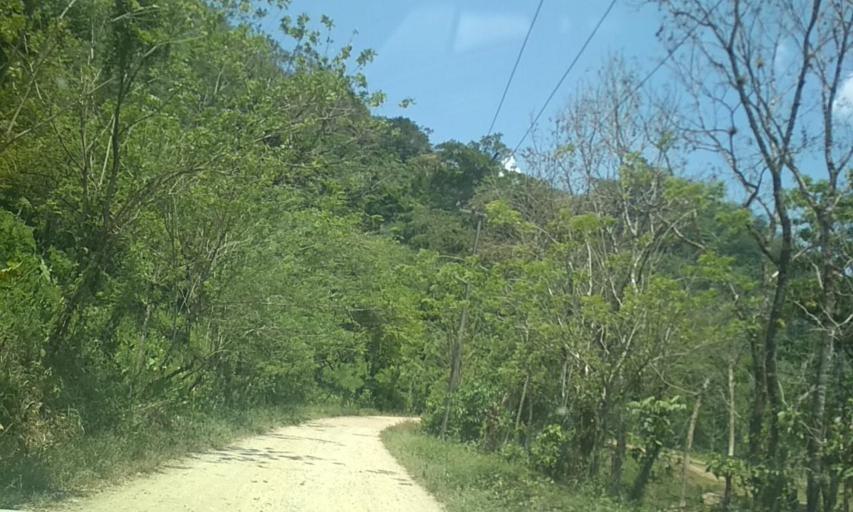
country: MX
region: Chiapas
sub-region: Tecpatan
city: Raudales Malpaso
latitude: 17.2817
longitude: -93.8232
